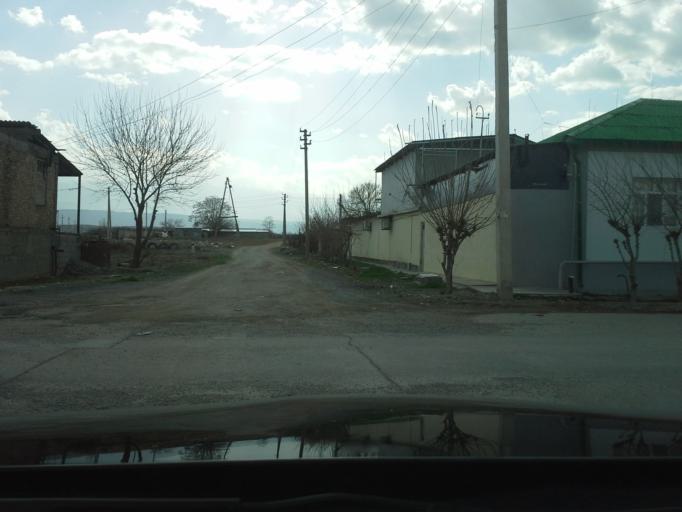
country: TM
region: Ahal
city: Abadan
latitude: 37.9870
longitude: 58.2811
